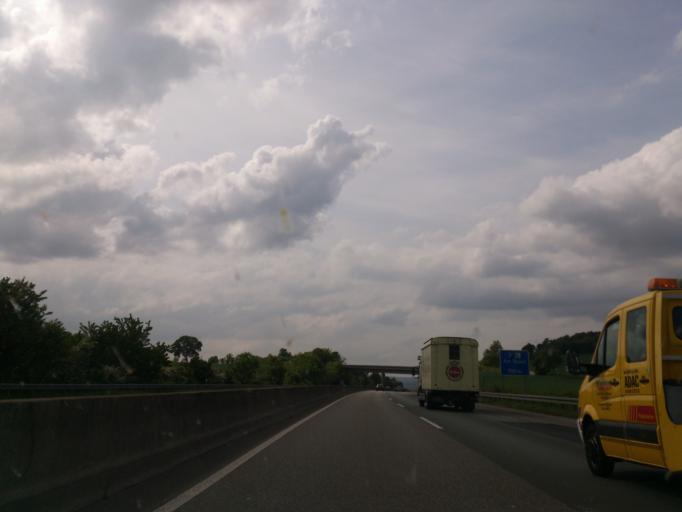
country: DE
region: Hesse
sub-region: Regierungsbezirk Kassel
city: Volkmarsen
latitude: 51.4805
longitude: 9.0423
